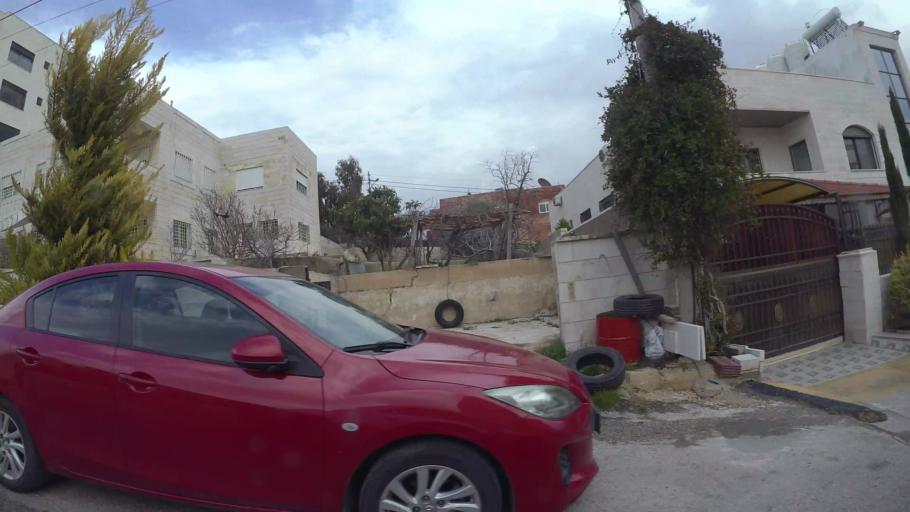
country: JO
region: Amman
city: Umm as Summaq
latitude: 31.8833
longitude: 35.8674
